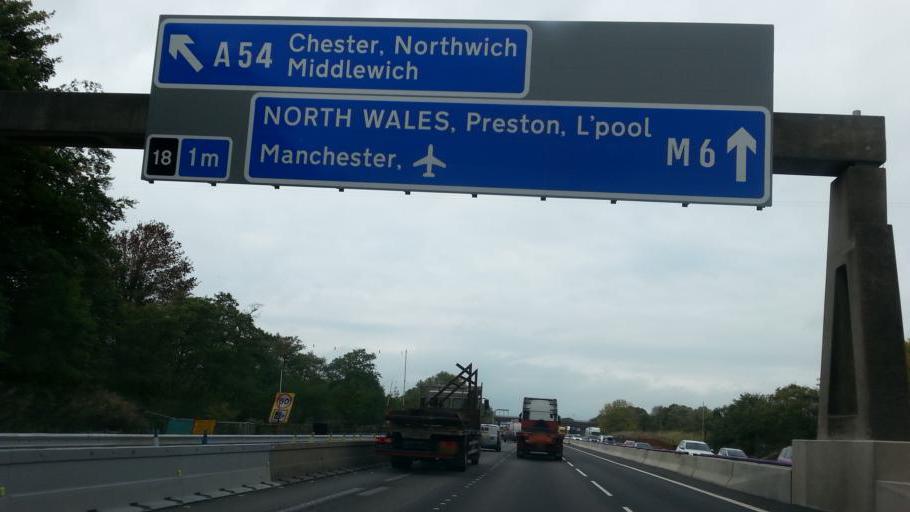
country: GB
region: England
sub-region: Cheshire East
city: Holmes Chapel
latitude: 53.1841
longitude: -2.3716
